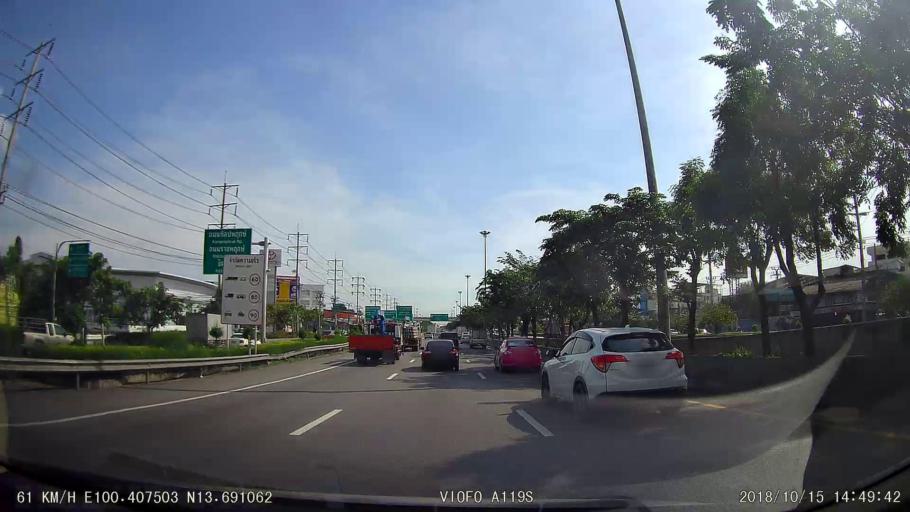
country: TH
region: Bangkok
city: Bang Khae
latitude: 13.6909
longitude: 100.4075
